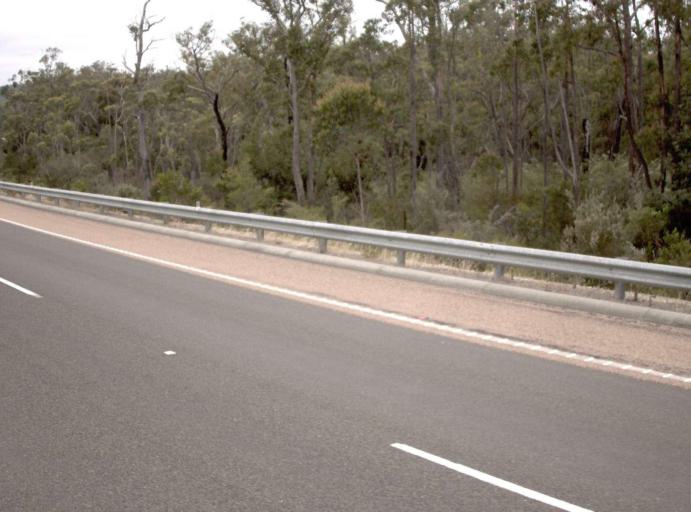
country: AU
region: Victoria
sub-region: East Gippsland
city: Lakes Entrance
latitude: -37.6949
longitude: 147.9968
